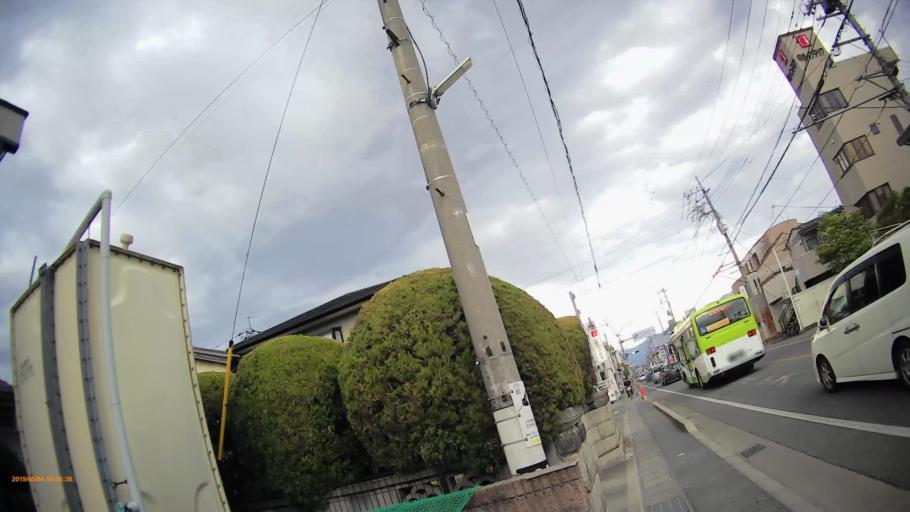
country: JP
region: Yamanashi
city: Kofu-shi
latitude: 35.6588
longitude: 138.5947
